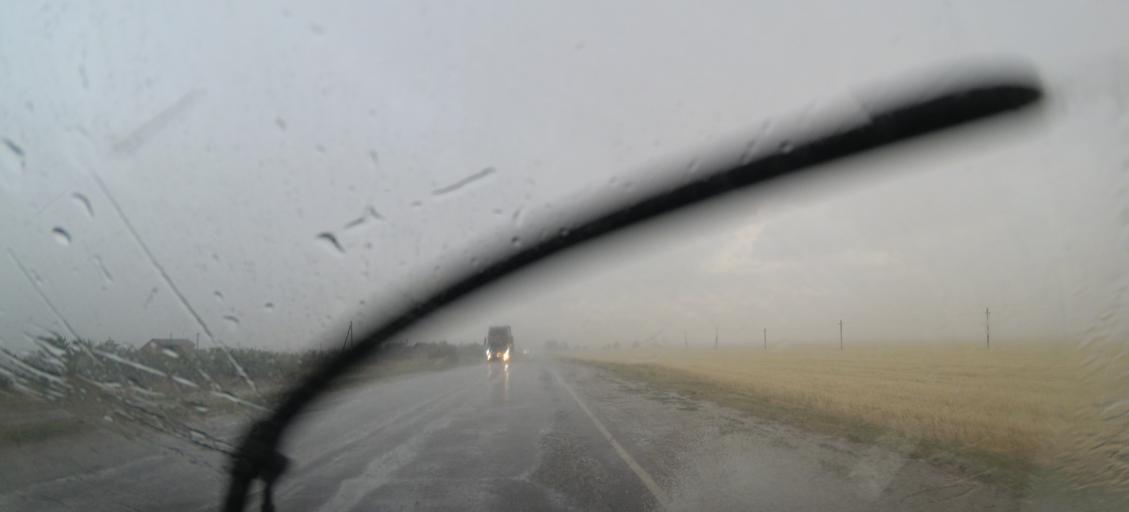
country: RU
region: Rostov
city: Proletarsk
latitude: 46.6822
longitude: 41.7164
